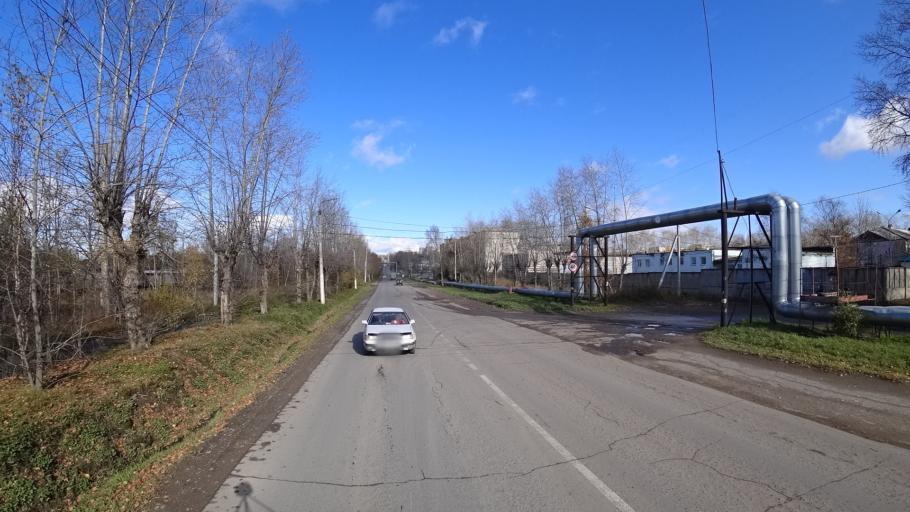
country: RU
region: Khabarovsk Krai
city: Amursk
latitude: 50.2242
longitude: 136.9014
